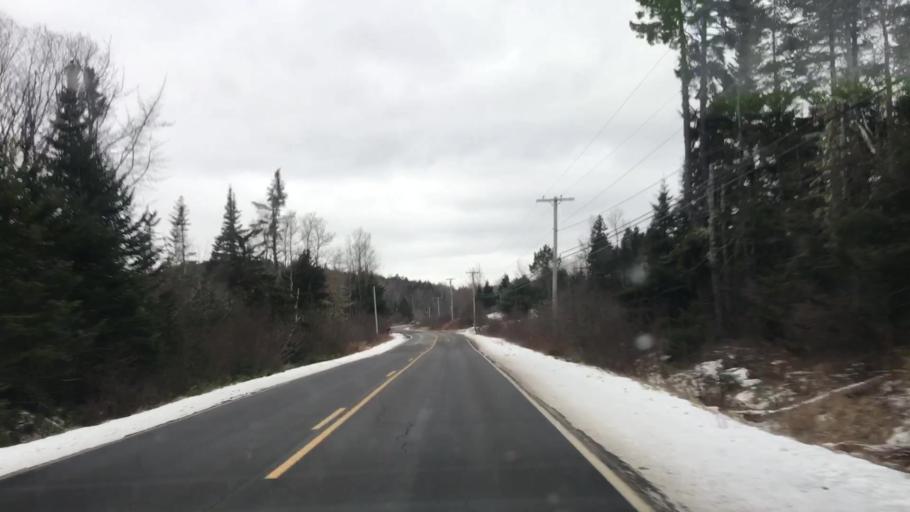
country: US
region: Maine
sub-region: Washington County
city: Machiasport
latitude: 44.7075
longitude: -67.3637
